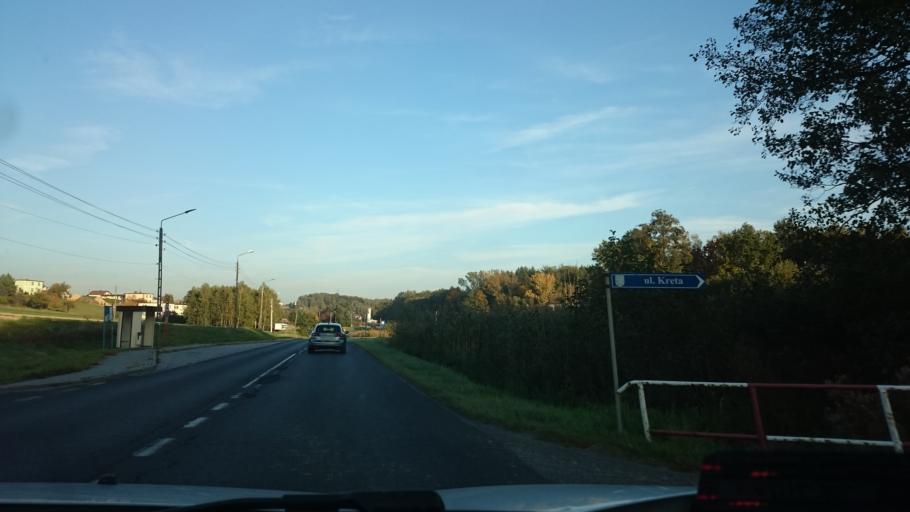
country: PL
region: Silesian Voivodeship
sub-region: Powiat wodzislawski
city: Marklowice
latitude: 50.0156
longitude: 18.5433
